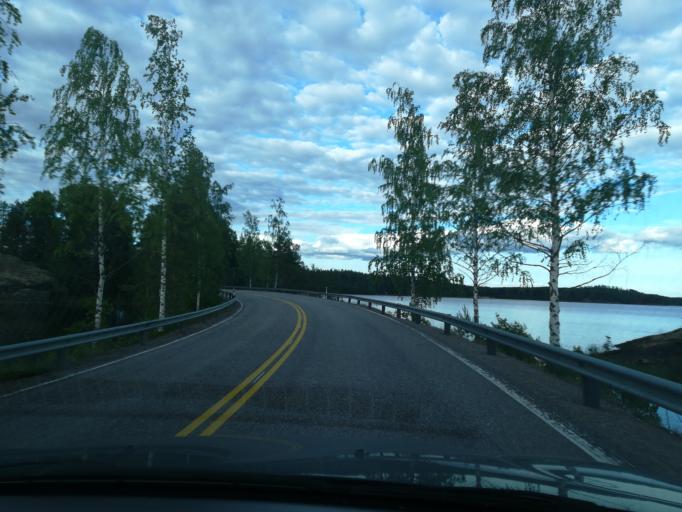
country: FI
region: Southern Savonia
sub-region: Mikkeli
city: Puumala
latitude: 61.5609
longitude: 27.9844
